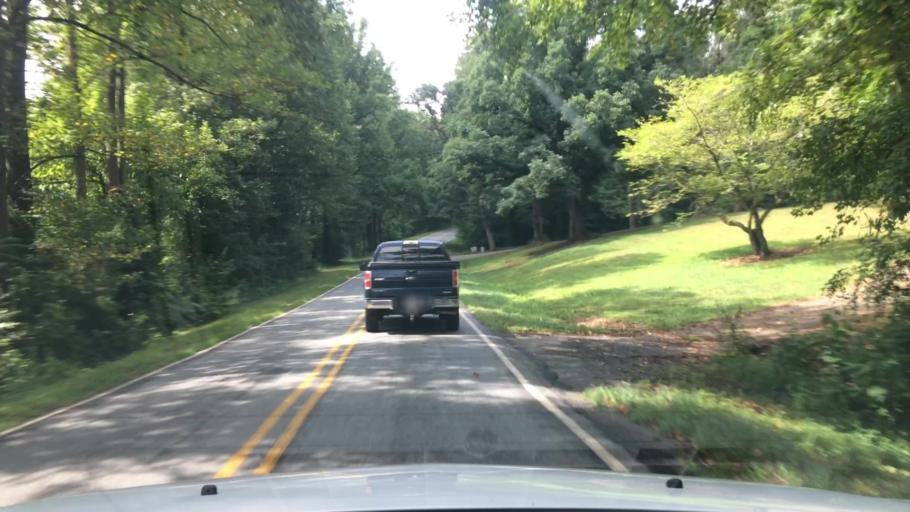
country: US
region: North Carolina
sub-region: Yadkin County
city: Jonesville
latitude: 36.1086
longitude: -80.8568
